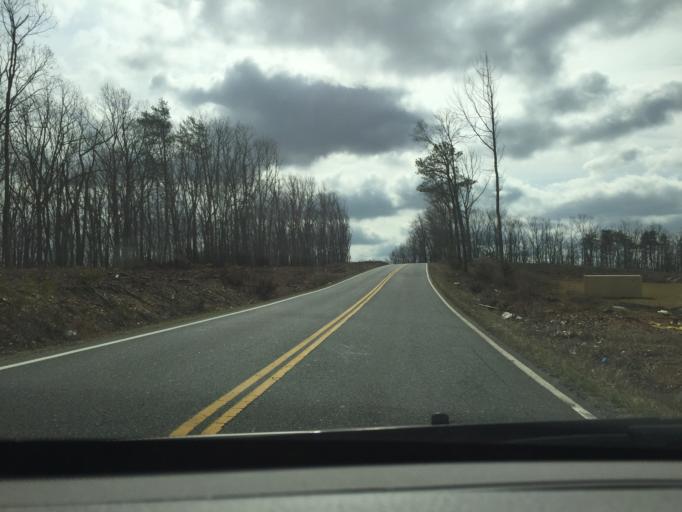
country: US
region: Virginia
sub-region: City of Lynchburg
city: West Lynchburg
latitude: 37.3362
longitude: -79.1709
